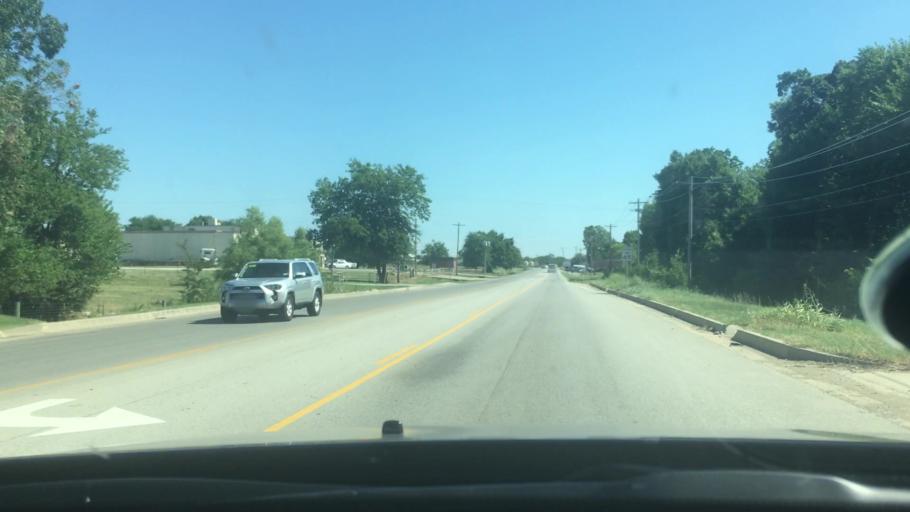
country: US
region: Oklahoma
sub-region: Bryan County
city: Durant
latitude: 33.9686
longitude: -96.3934
